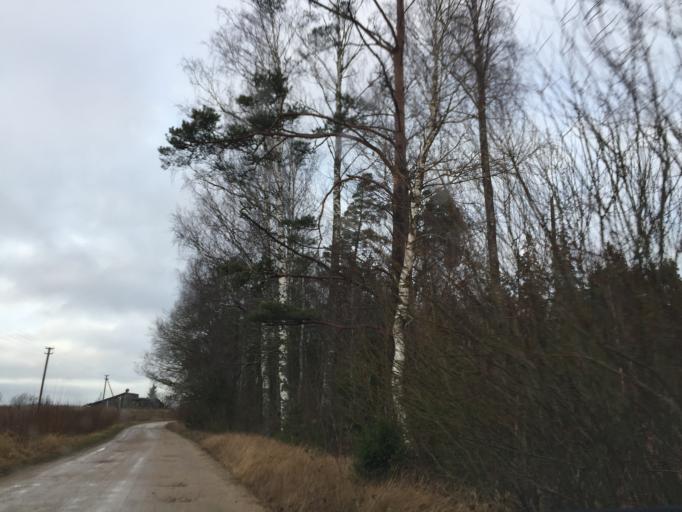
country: LV
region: Vainode
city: Vainode
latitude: 56.6044
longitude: 21.8005
